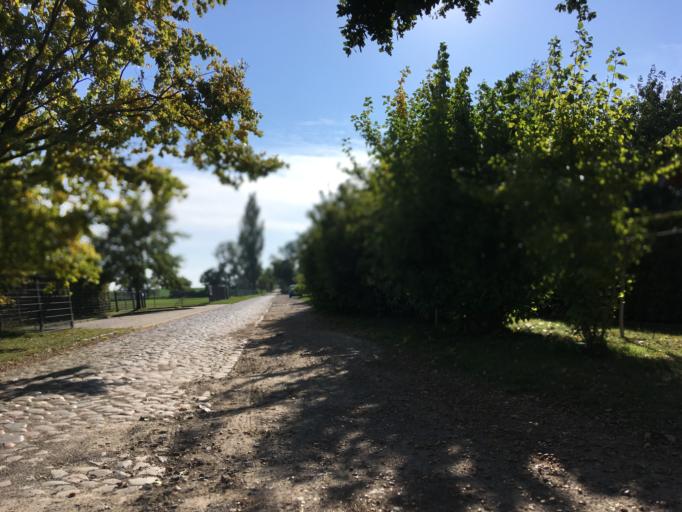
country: DE
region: Brandenburg
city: Altlandsberg
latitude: 52.5587
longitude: 13.7292
